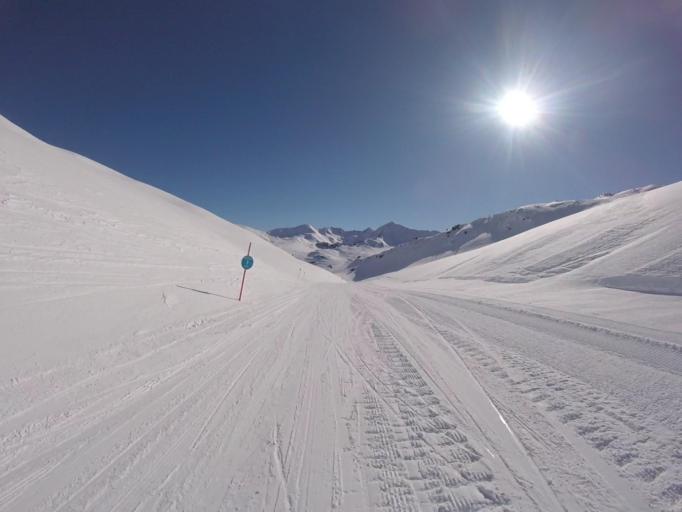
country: ES
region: Catalonia
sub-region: Provincia de Lleida
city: Vielha
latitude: 42.7248
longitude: 0.9408
